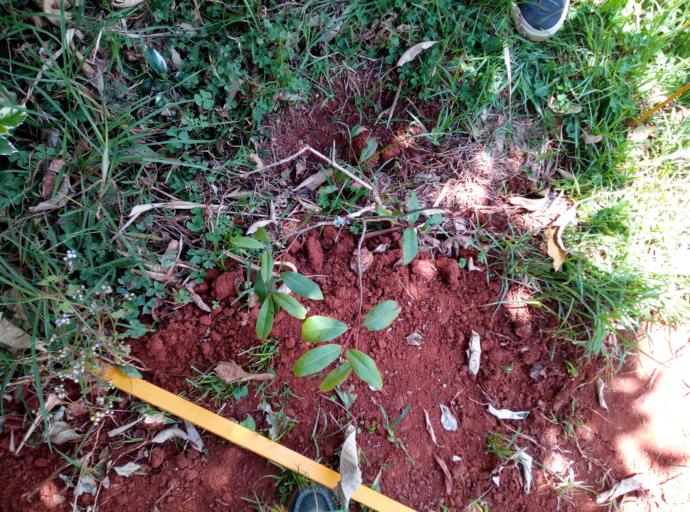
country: KE
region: Kirinyaga
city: Keruguya
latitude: -0.4755
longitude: 37.1405
